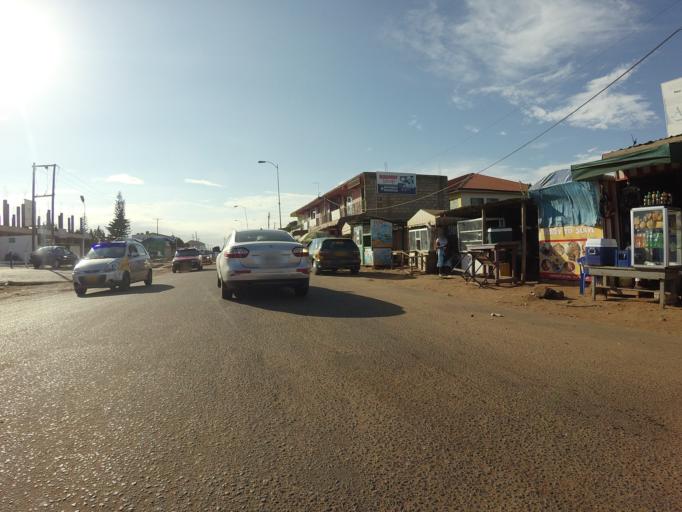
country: GH
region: Greater Accra
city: Tema
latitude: 5.6463
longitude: -0.0589
